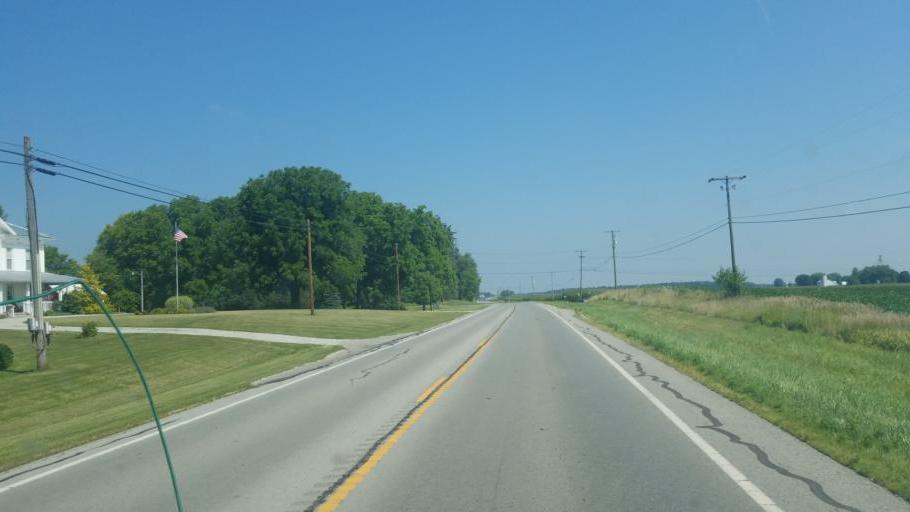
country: US
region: Ohio
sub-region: Hardin County
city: Kenton
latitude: 40.6732
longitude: -83.6119
